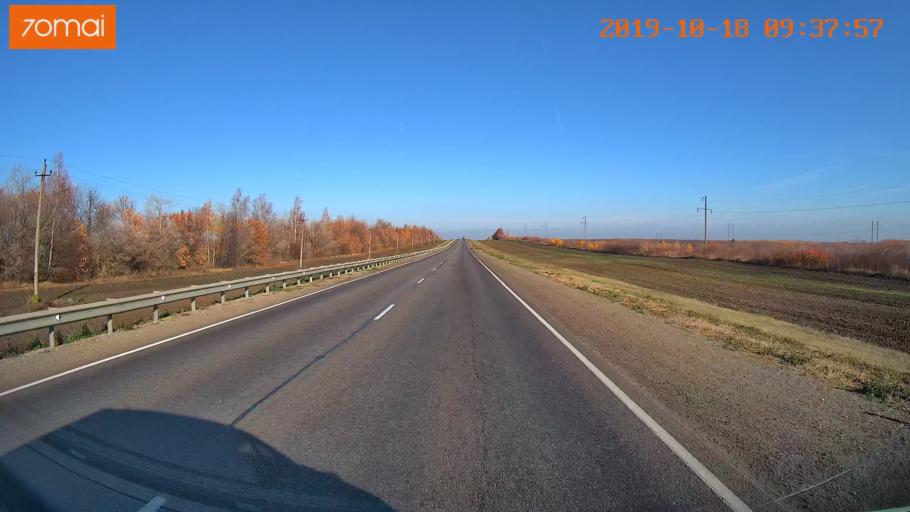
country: RU
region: Tula
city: Yefremov
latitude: 53.2304
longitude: 38.1390
